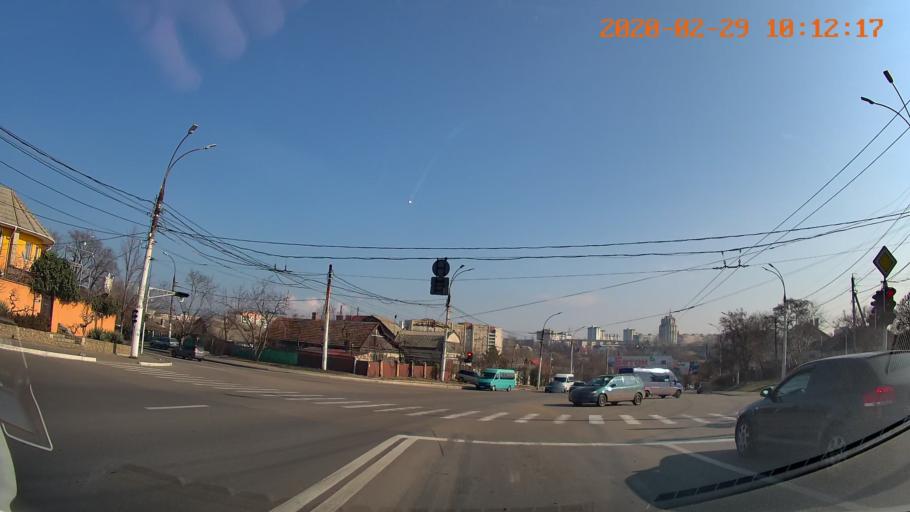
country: MD
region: Telenesti
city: Tiraspolul Nou
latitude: 46.8379
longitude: 29.6473
